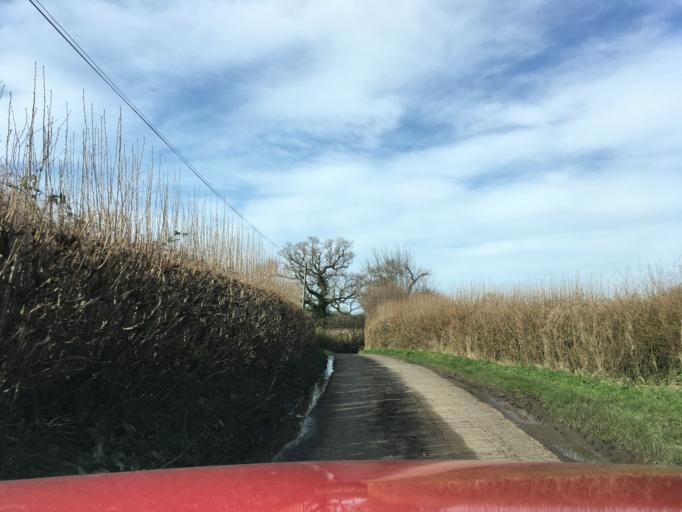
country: GB
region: England
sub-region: Wiltshire
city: Nettleton
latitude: 51.5238
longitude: -2.2478
